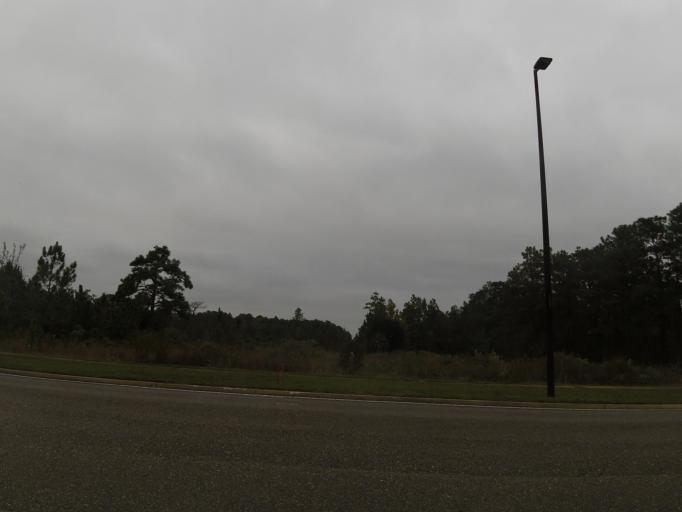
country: US
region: Florida
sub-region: Duval County
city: Baldwin
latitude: 30.2336
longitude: -81.8864
